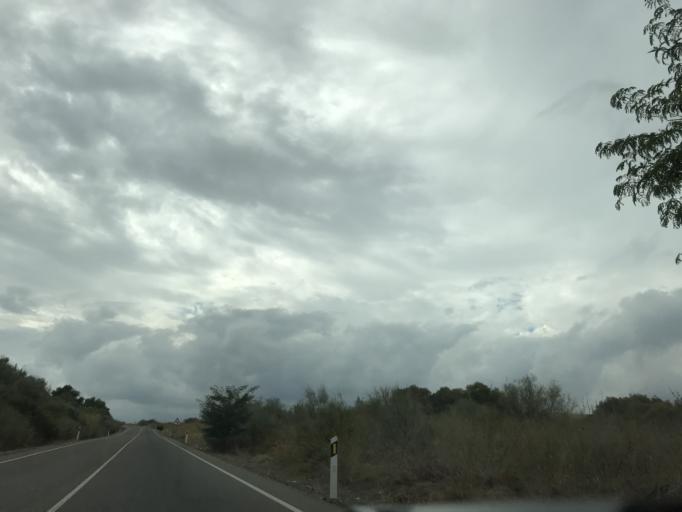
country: ES
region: Andalusia
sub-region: Provincia de Sevilla
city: Tocina
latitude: 37.6404
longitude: -5.7480
